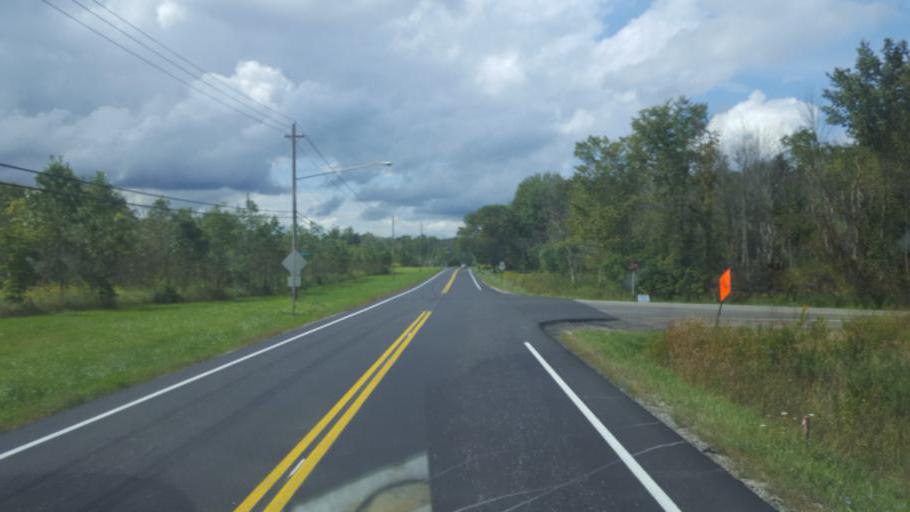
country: US
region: Ohio
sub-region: Geauga County
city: Burton
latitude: 41.4570
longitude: -81.1326
